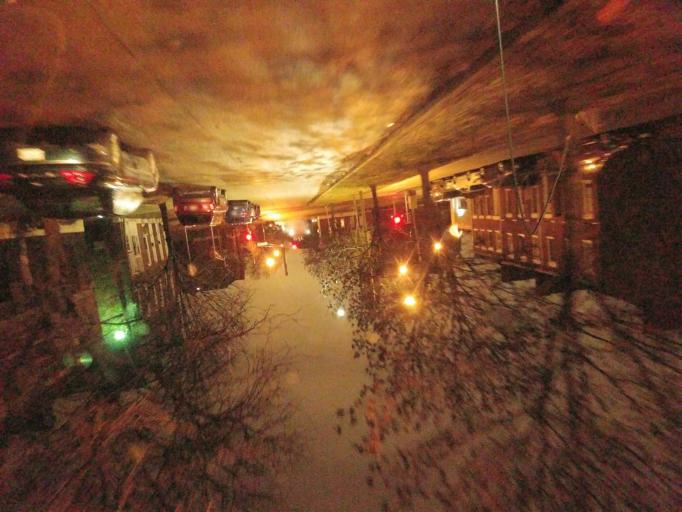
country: US
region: Missouri
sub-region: City of Saint Louis
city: St. Louis
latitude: 38.6478
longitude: -90.1976
